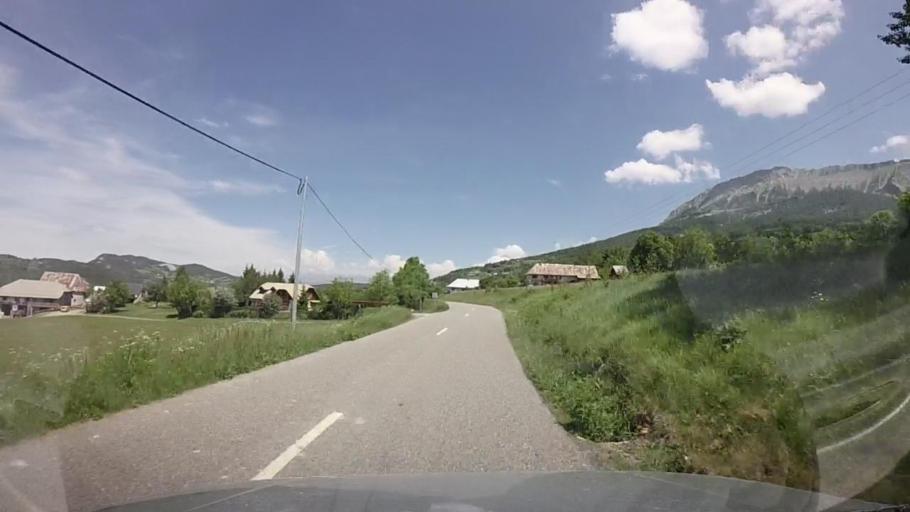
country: FR
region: Provence-Alpes-Cote d'Azur
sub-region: Departement des Alpes-de-Haute-Provence
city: Seyne-les-Alpes
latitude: 44.3854
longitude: 6.3467
